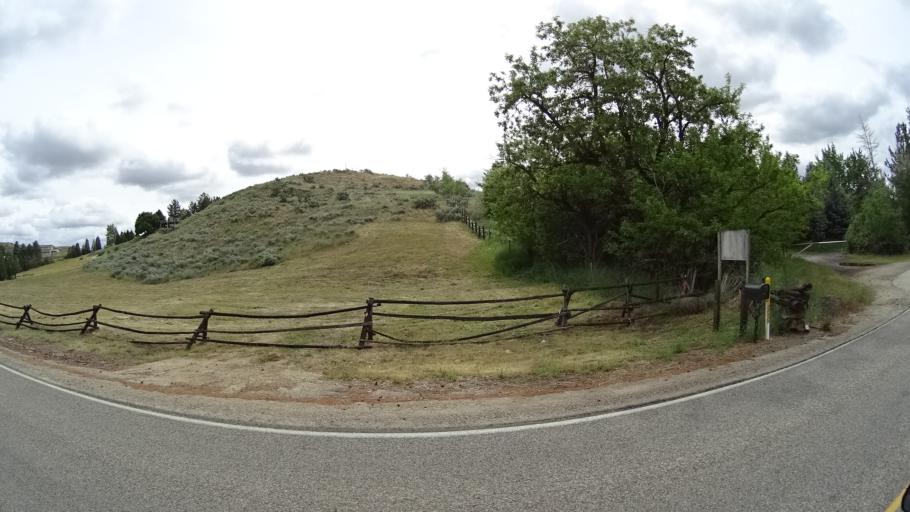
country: US
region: Idaho
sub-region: Ada County
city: Eagle
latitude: 43.7353
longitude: -116.3575
